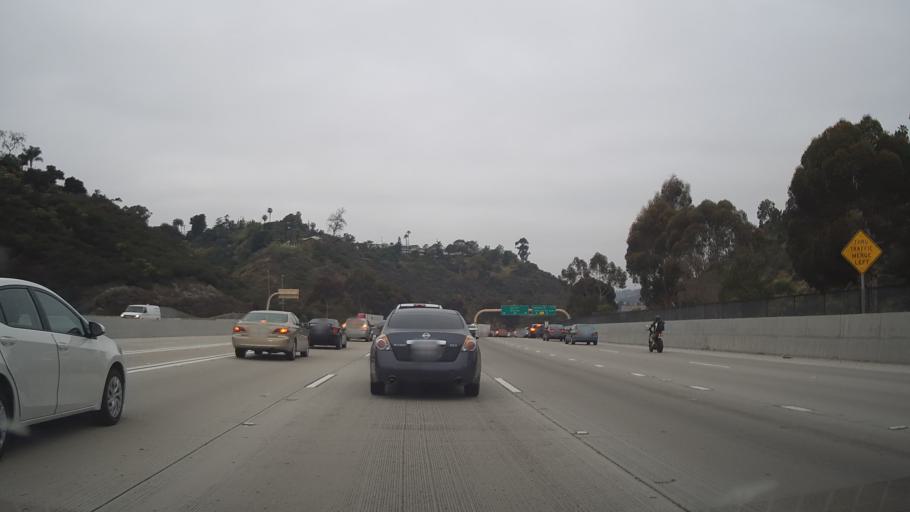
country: US
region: California
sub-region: San Diego County
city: San Diego
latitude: 32.7700
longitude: -117.1117
